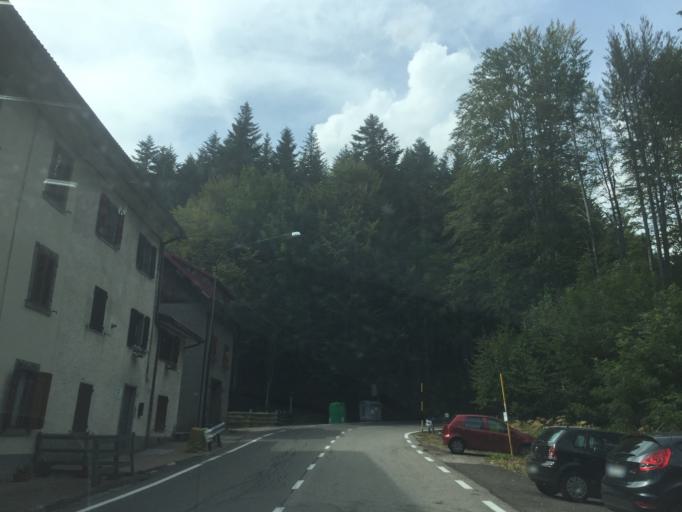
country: IT
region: Tuscany
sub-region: Provincia di Pistoia
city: Abetone
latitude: 44.1257
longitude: 10.6964
